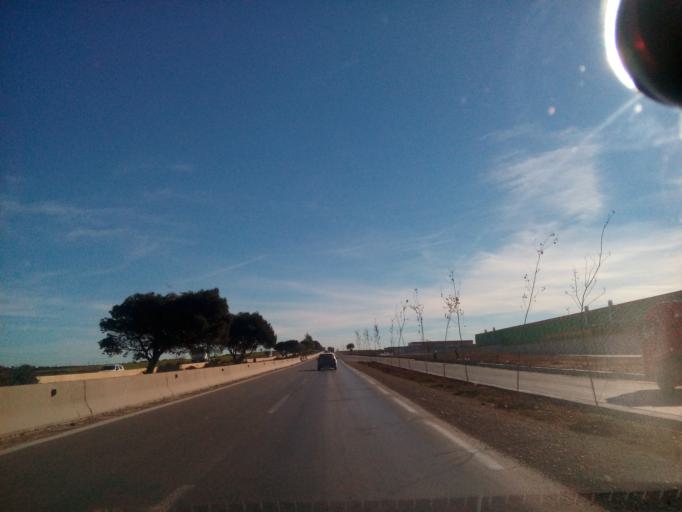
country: DZ
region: Oran
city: Ain el Bya
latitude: 35.7753
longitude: -0.2550
